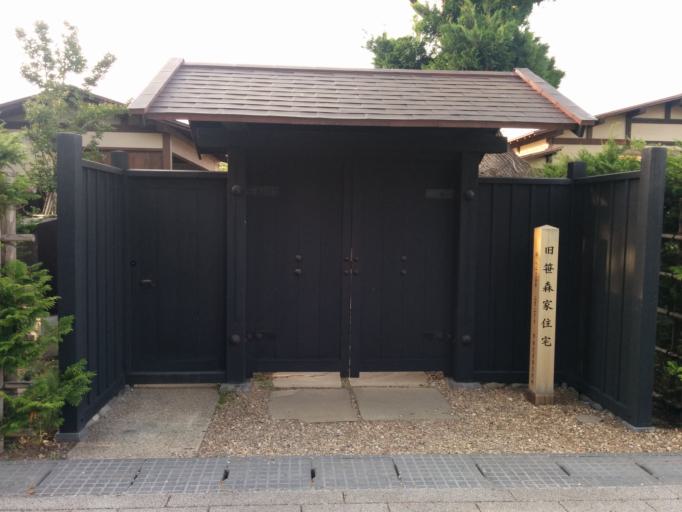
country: JP
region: Aomori
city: Hirosaki
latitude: 40.6128
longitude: 140.4656
